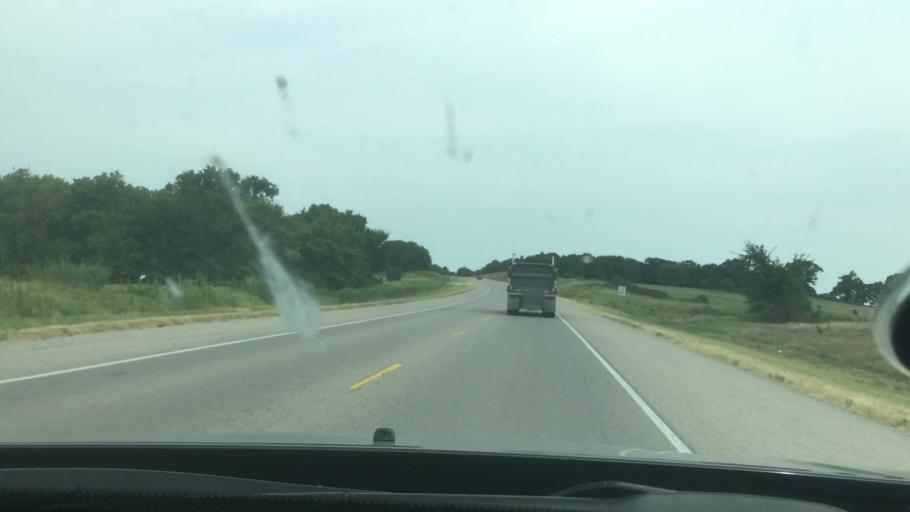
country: US
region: Oklahoma
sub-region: Pontotoc County
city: Ada
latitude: 34.6720
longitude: -96.5704
